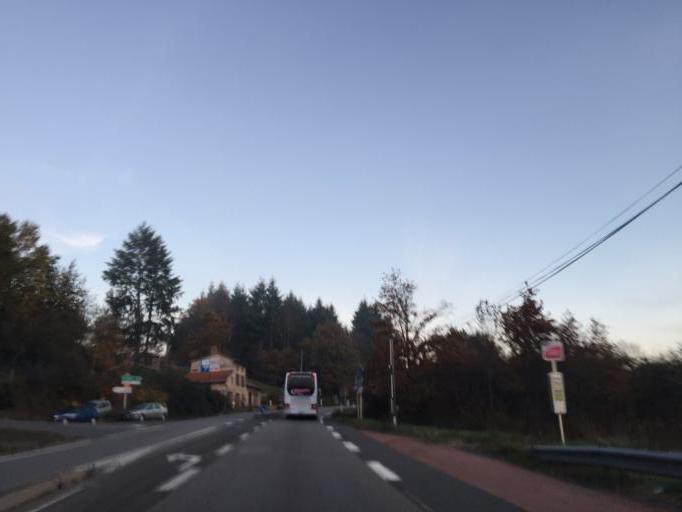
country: FR
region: Rhone-Alpes
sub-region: Departement de la Loire
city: Neulise
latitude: 45.8632
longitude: 4.1754
